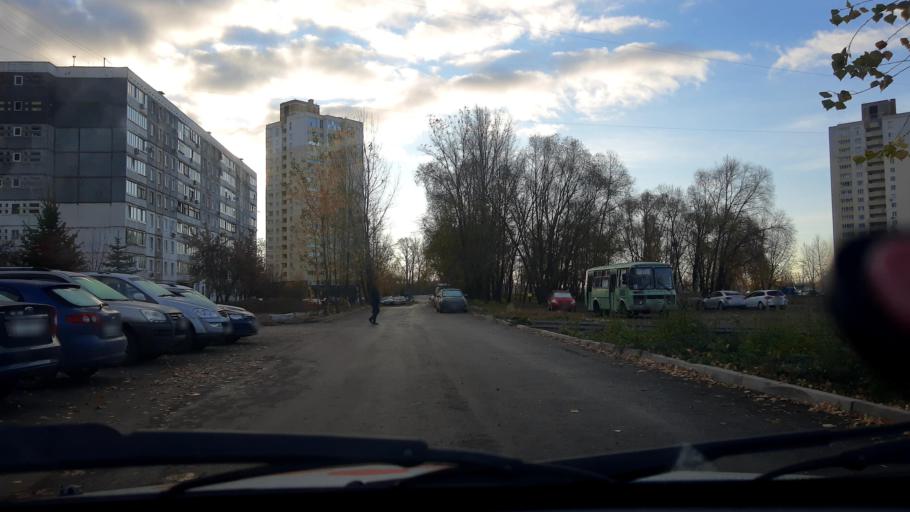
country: RU
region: Bashkortostan
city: Ufa
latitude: 54.7667
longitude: 56.0750
